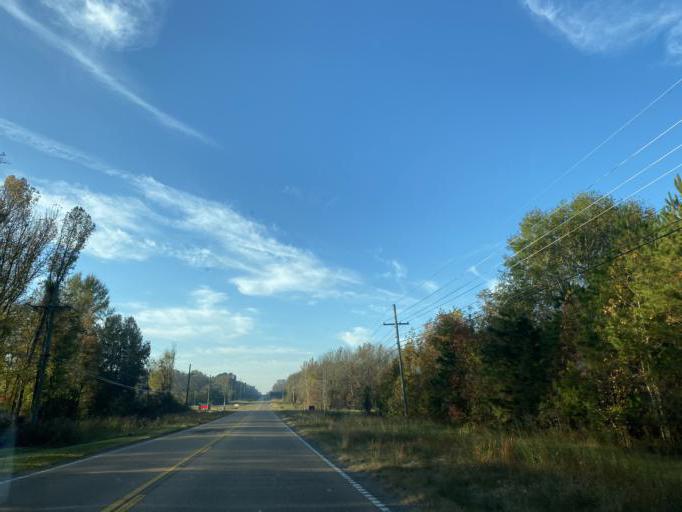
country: US
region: Mississippi
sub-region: Madison County
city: Madison
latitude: 32.5017
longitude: -90.0907
